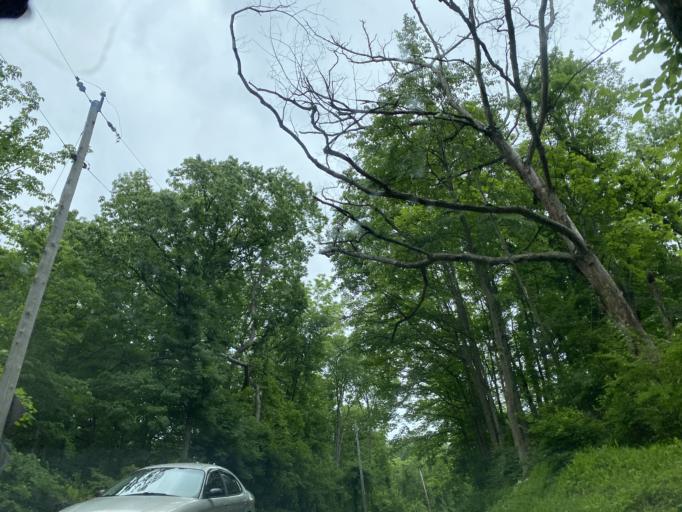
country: US
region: Kentucky
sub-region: Campbell County
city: Dayton
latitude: 39.1024
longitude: -84.4596
